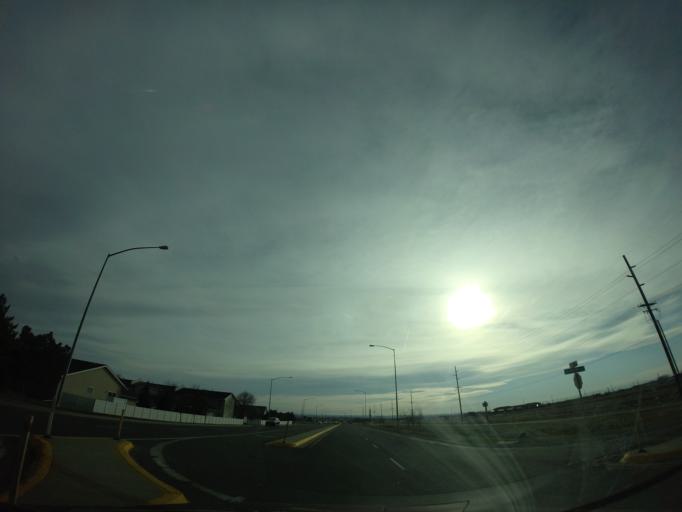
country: US
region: Montana
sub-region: Yellowstone County
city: Billings
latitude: 45.7594
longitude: -108.6177
